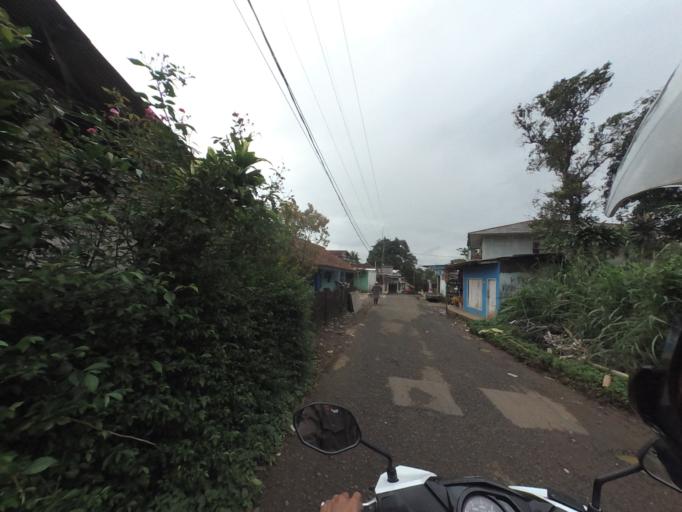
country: ID
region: West Java
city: Bogor
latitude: -6.6358
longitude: 106.7295
